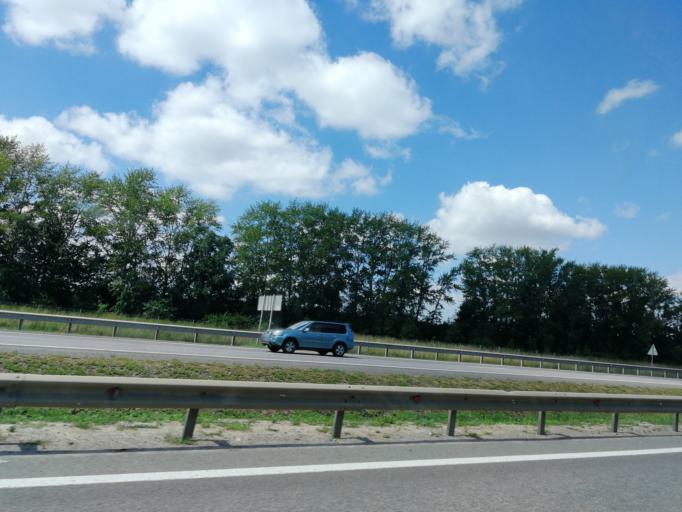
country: RU
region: Tula
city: Dubovka
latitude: 53.9188
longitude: 38.0423
